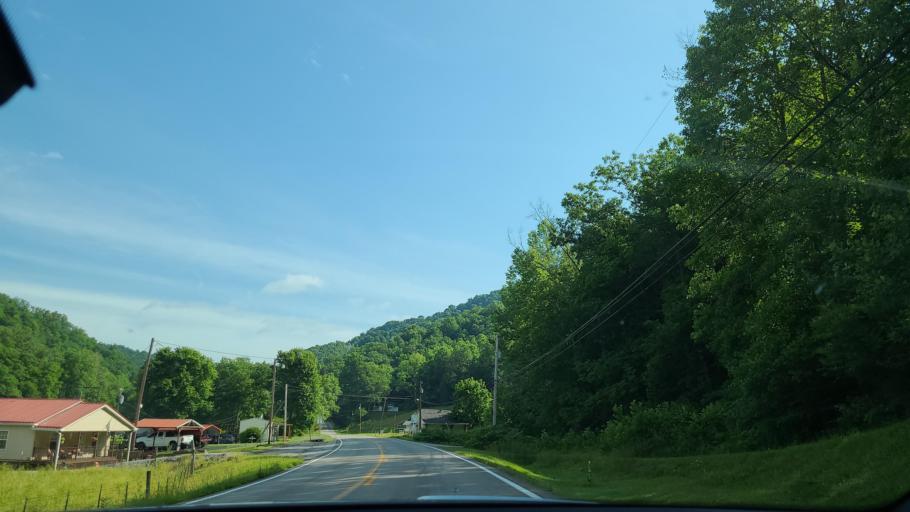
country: US
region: Kentucky
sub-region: Bell County
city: Pineville
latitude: 36.7293
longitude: -83.7983
